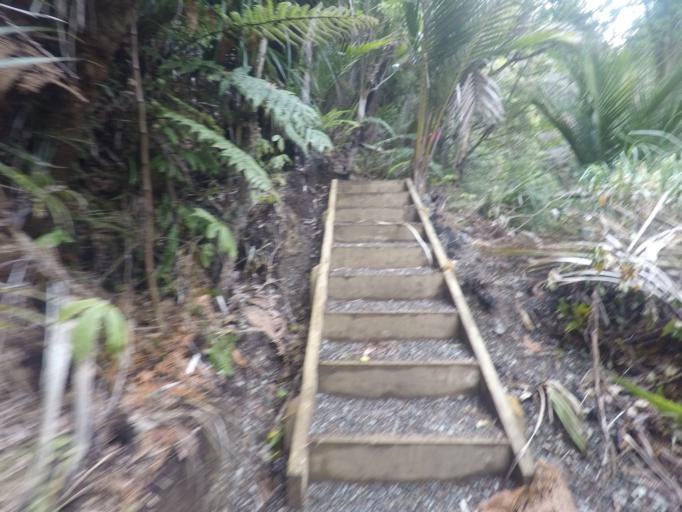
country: NZ
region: Auckland
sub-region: Auckland
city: Titirangi
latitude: -36.9999
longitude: 174.5452
